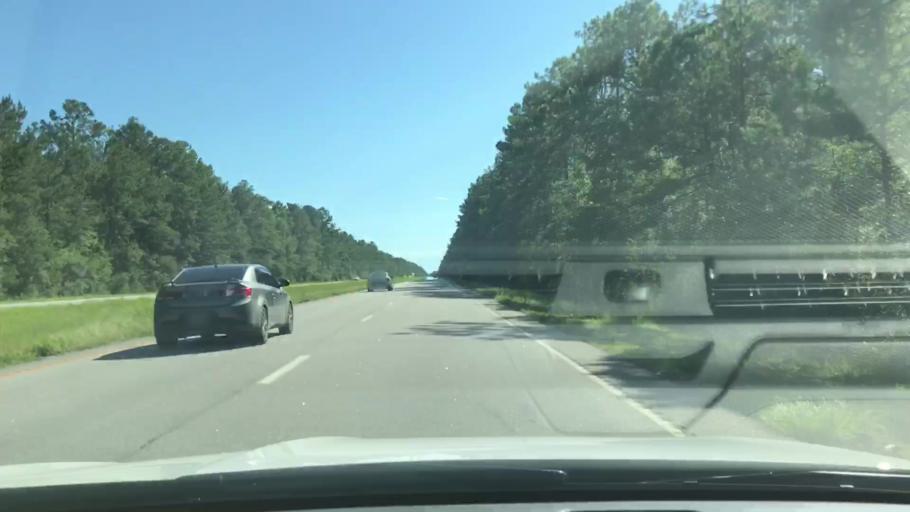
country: US
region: South Carolina
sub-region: Charleston County
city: Awendaw
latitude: 33.1586
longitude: -79.4278
